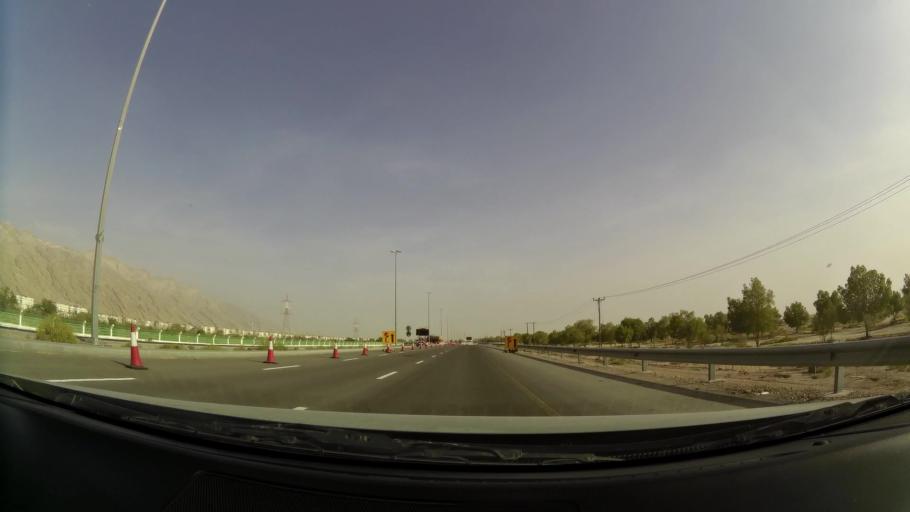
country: AE
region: Abu Dhabi
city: Al Ain
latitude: 24.0799
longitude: 55.7265
